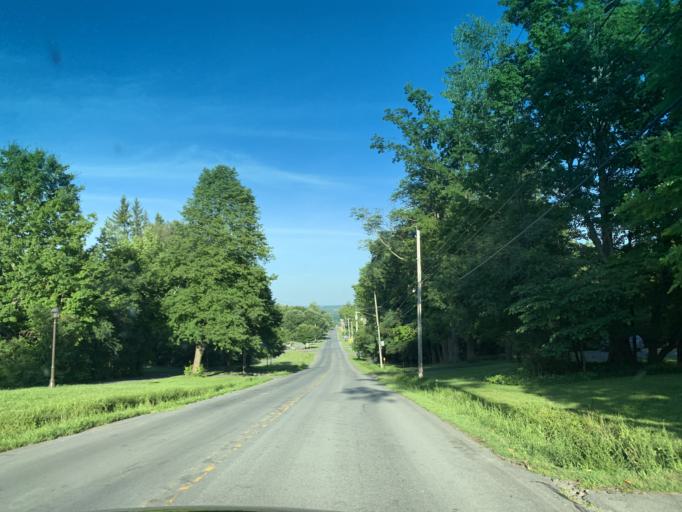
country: US
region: New York
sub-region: Oneida County
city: Clinton
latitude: 43.0509
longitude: -75.4123
